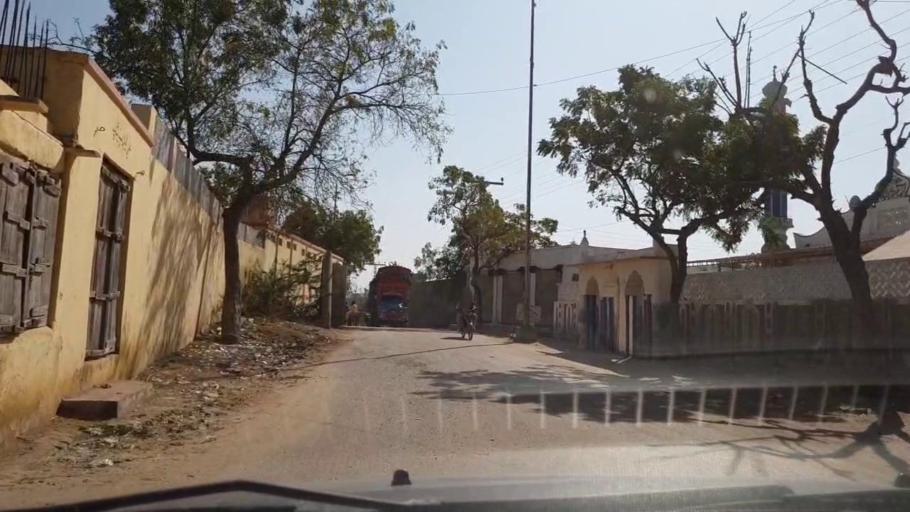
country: PK
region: Sindh
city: Diplo
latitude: 24.4710
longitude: 69.5790
